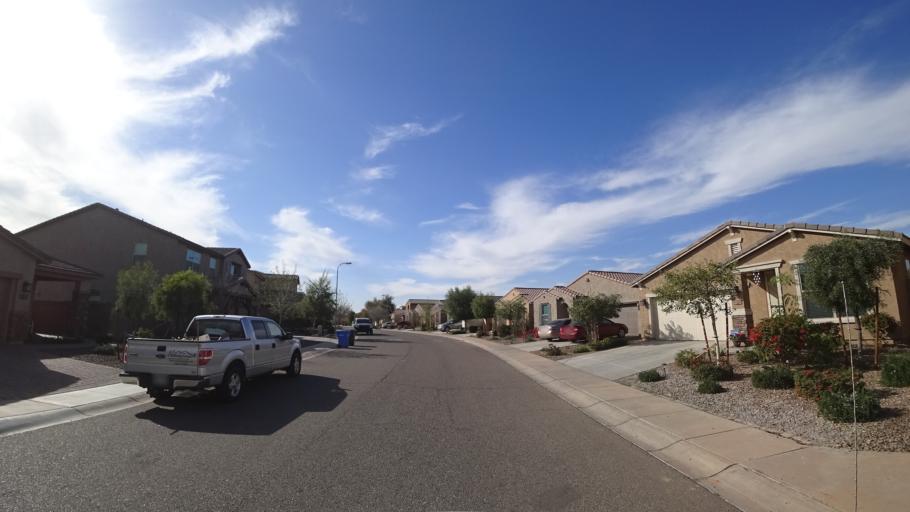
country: US
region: Arizona
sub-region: Maricopa County
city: Tolleson
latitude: 33.4242
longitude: -112.2825
